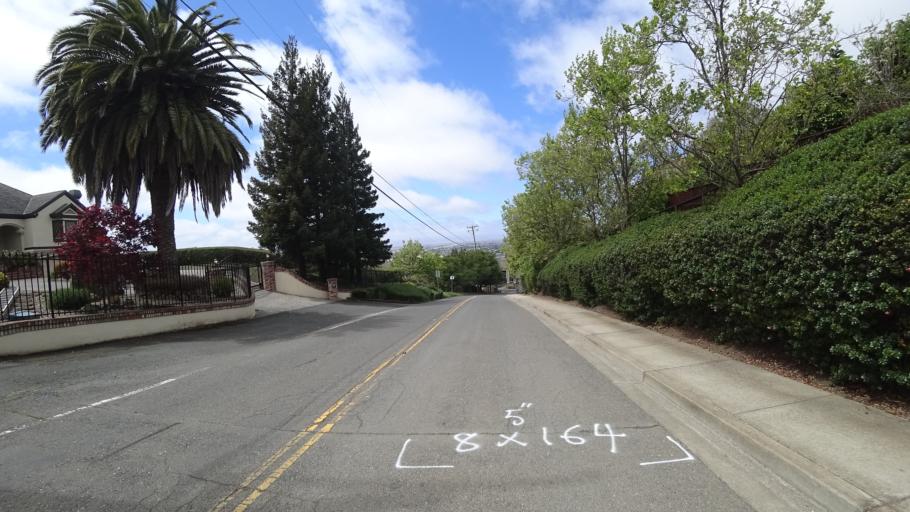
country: US
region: California
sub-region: Alameda County
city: Union City
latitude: 37.6281
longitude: -122.0340
